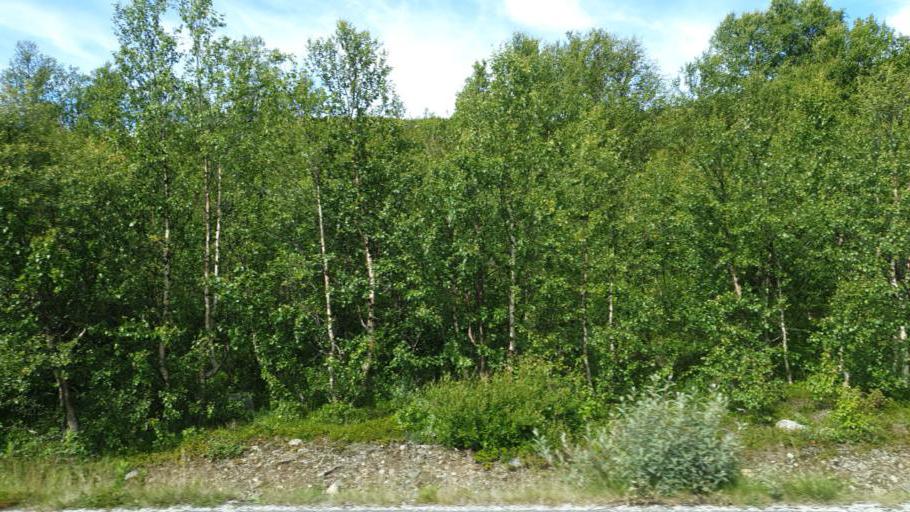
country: NO
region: Oppland
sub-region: Vaga
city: Vagamo
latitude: 61.5179
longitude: 8.8628
